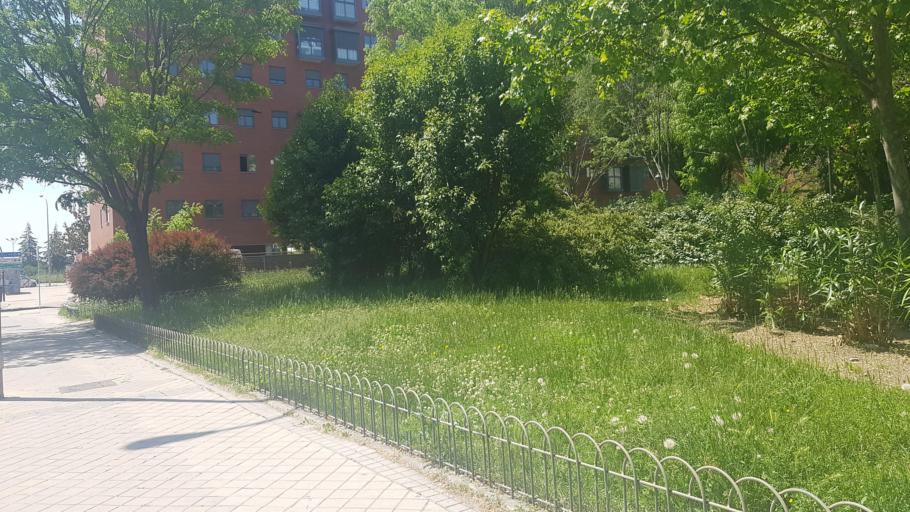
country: ES
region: Madrid
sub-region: Provincia de Madrid
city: Villaverde
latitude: 40.3675
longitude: -3.7123
